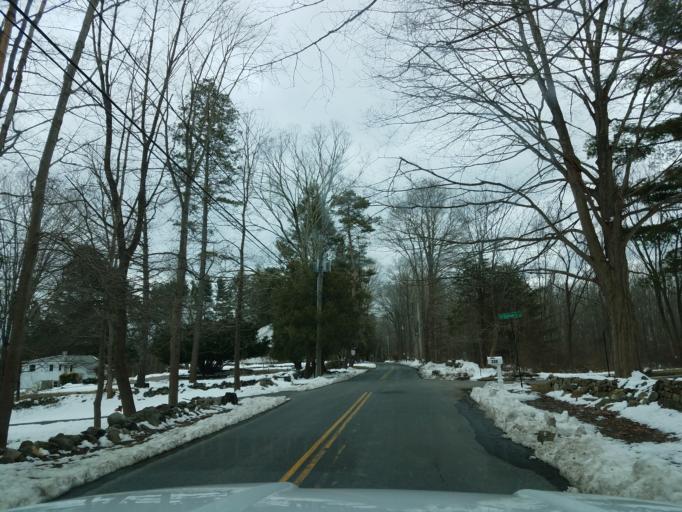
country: US
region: Connecticut
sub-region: Litchfield County
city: New Milford
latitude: 41.6192
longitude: -73.4307
